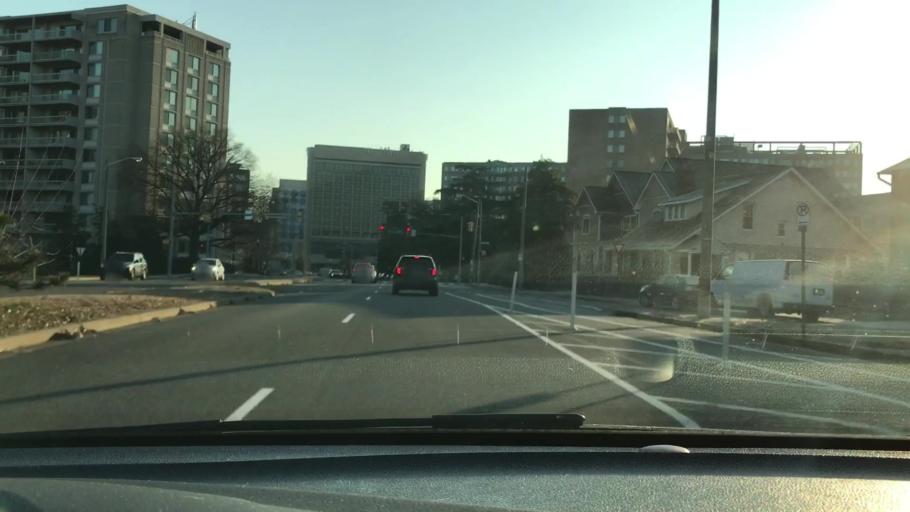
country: US
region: Washington, D.C.
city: Washington, D.C.
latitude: 38.8573
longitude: -77.0568
